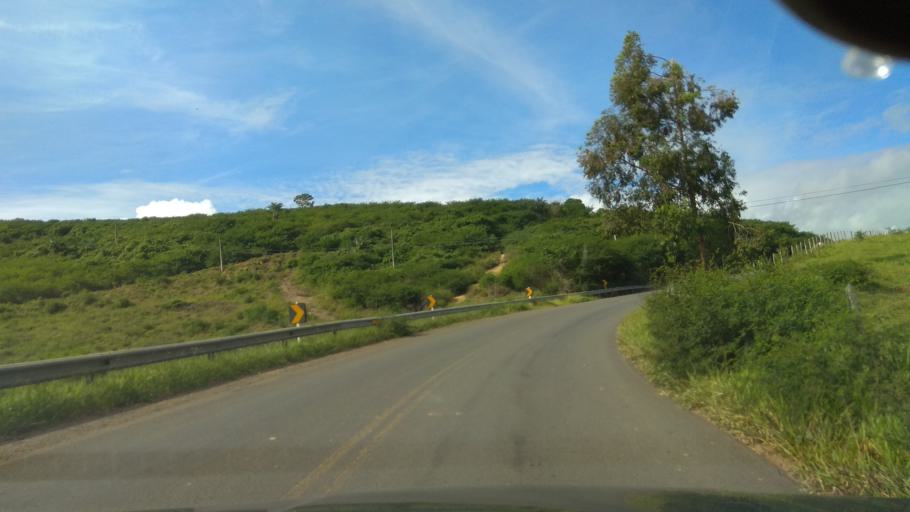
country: BR
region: Bahia
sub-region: Ubaira
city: Ubaira
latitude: -13.2654
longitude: -39.6593
